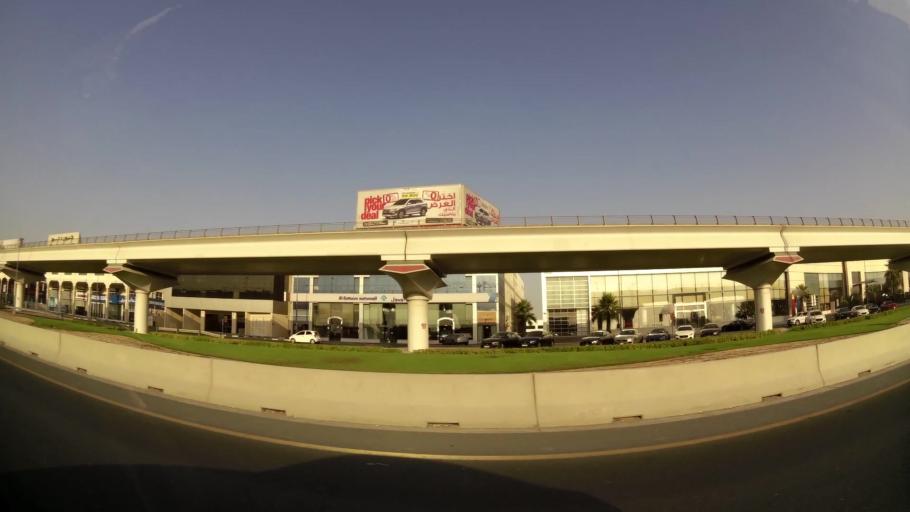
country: AE
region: Dubai
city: Dubai
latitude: 25.1432
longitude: 55.2201
